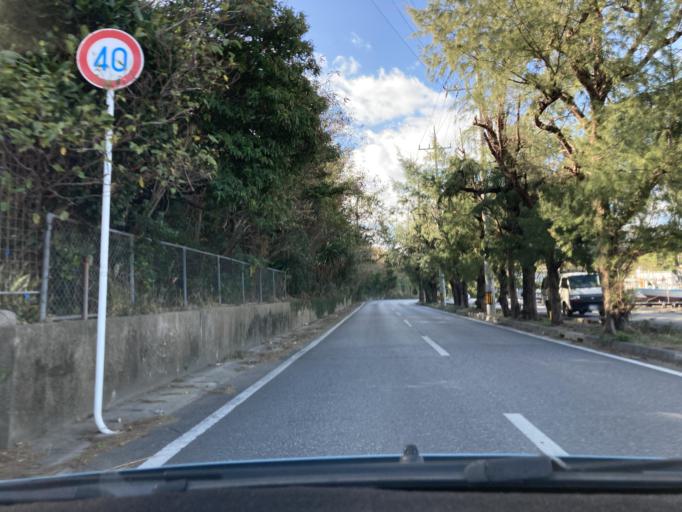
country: JP
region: Okinawa
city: Katsuren-haebaru
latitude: 26.3189
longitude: 127.9167
